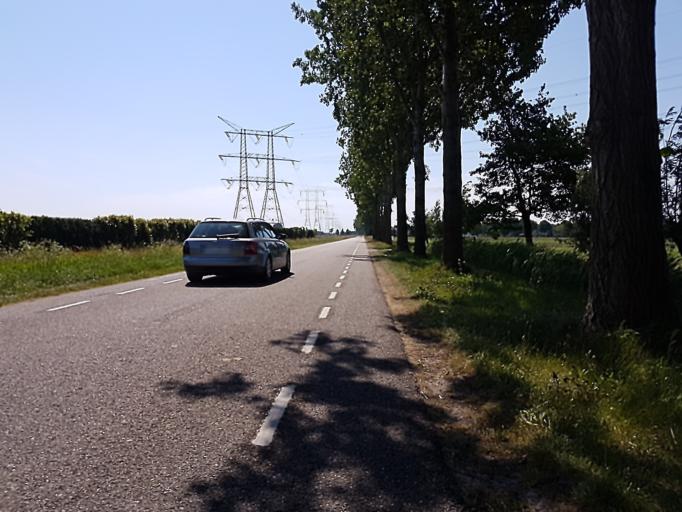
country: NL
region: North Brabant
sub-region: Gemeente Dongen
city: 's Gravenmoer
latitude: 51.6534
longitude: 4.9878
